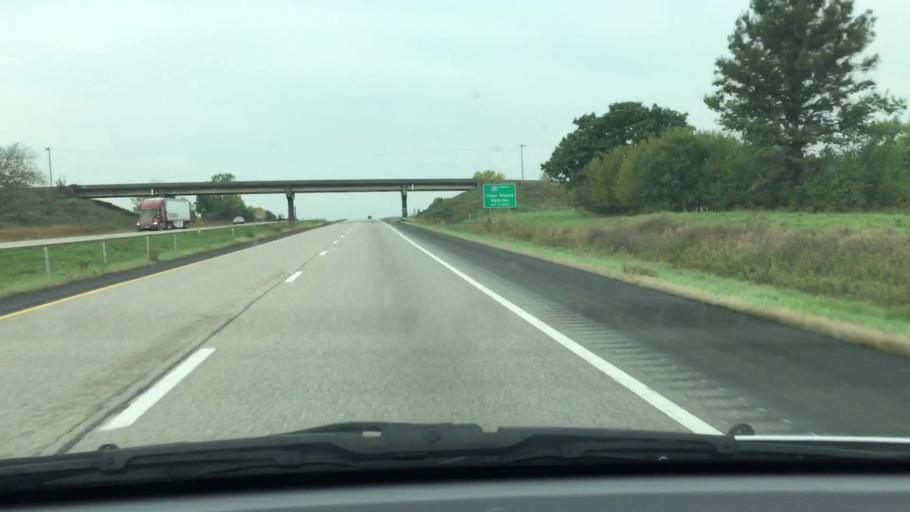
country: US
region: Iowa
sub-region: Muscatine County
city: West Liberty
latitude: 41.6583
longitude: -91.2036
